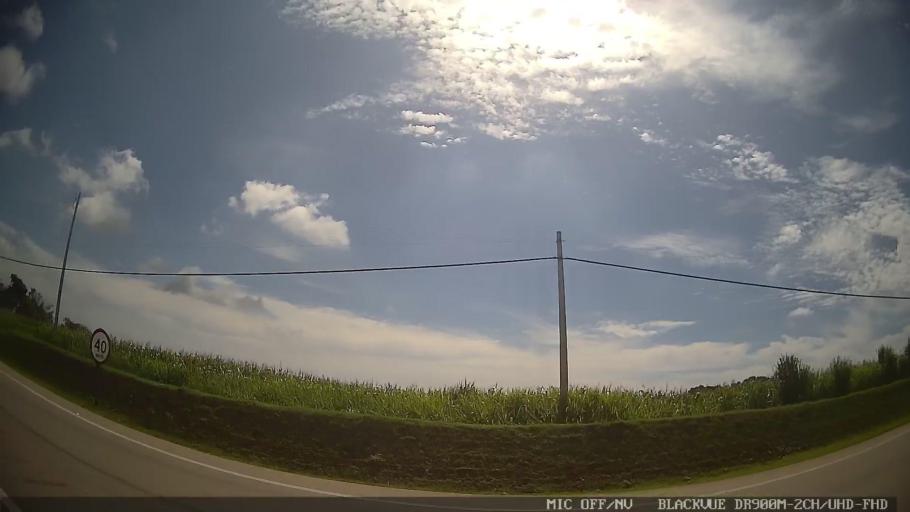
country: BR
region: Sao Paulo
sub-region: Tiete
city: Tiete
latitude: -23.1213
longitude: -47.7002
